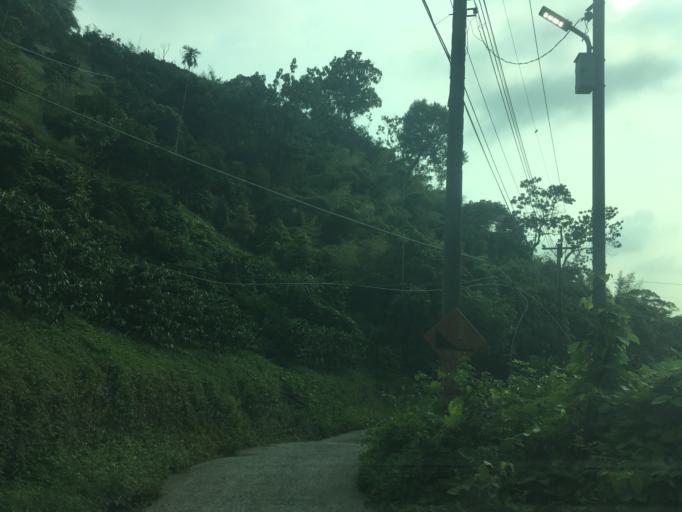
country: TW
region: Taiwan
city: Fengyuan
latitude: 24.2290
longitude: 120.7717
